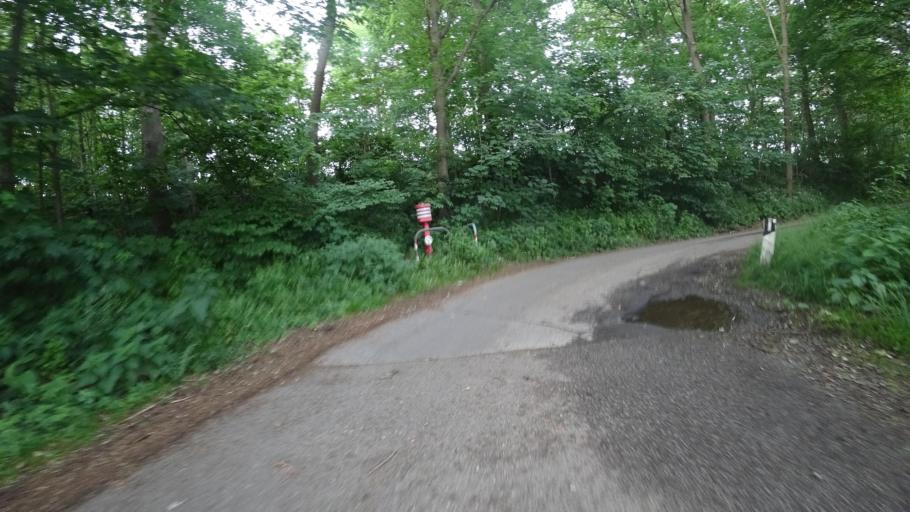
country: DE
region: North Rhine-Westphalia
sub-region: Regierungsbezirk Detmold
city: Guetersloh
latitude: 51.8744
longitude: 8.4179
